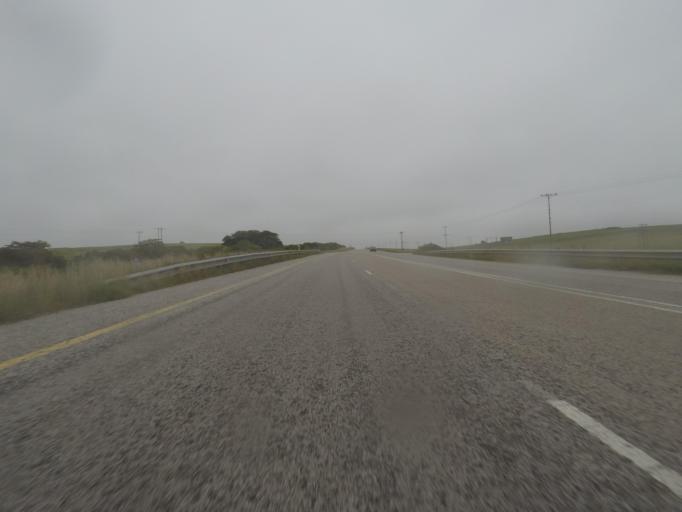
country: ZA
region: Eastern Cape
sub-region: Cacadu District Municipality
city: Grahamstown
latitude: -33.6237
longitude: 26.2938
